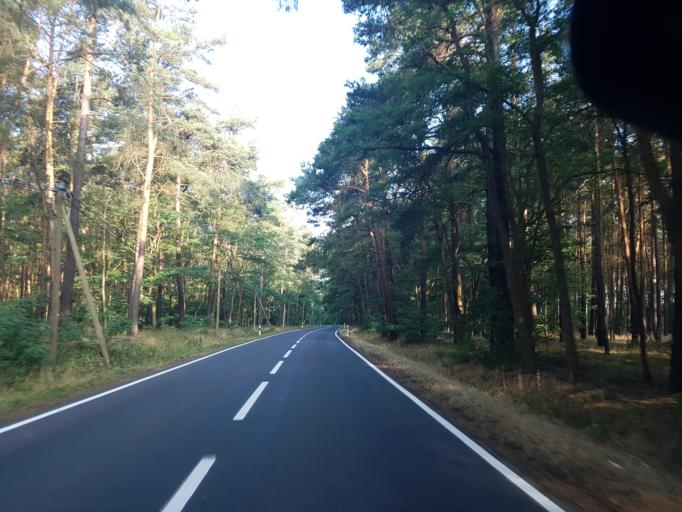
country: DE
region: Brandenburg
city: Ihlow
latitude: 51.8119
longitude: 13.2529
